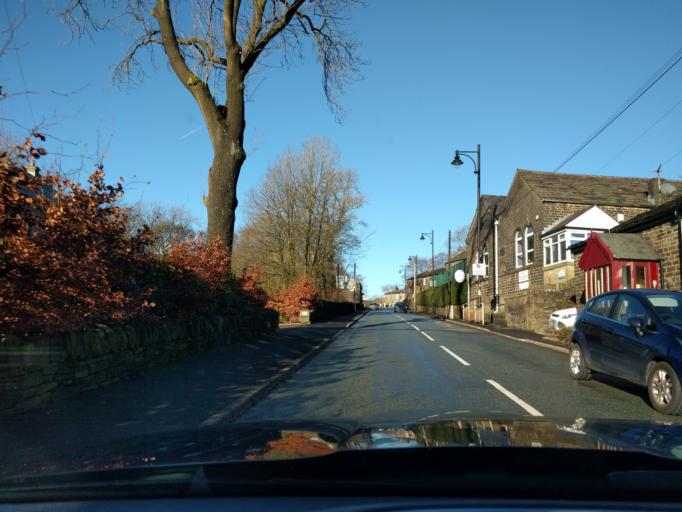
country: GB
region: England
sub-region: Borough of Oldham
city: Delph
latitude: 53.5906
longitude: -2.0391
